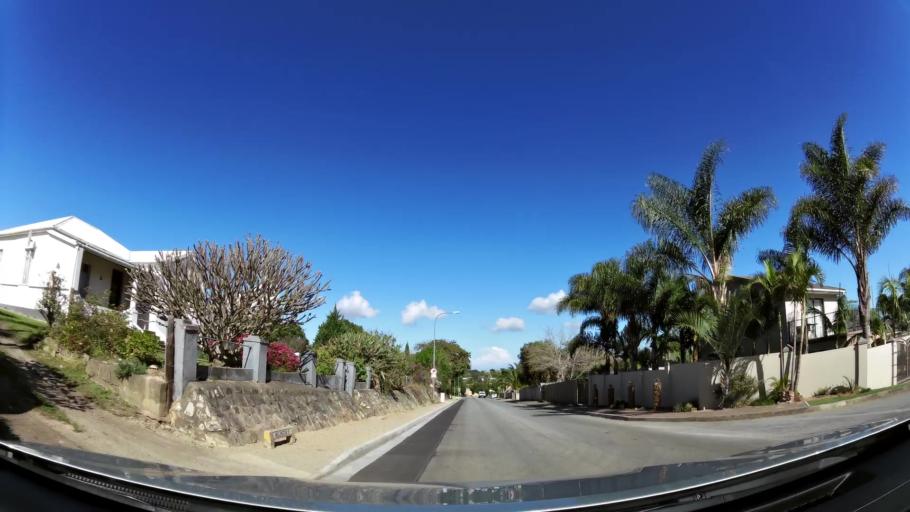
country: ZA
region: Western Cape
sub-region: Eden District Municipality
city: George
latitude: -33.9471
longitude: 22.4731
